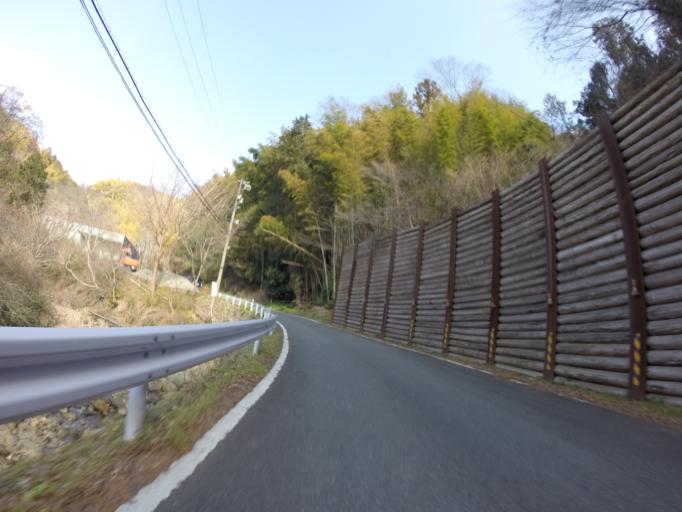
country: JP
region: Shizuoka
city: Shizuoka-shi
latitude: 35.0668
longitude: 138.4953
